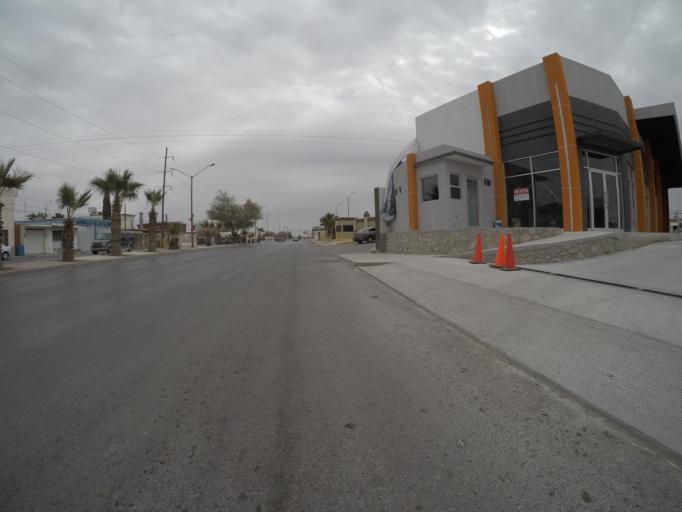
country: MX
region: Chihuahua
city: Ciudad Juarez
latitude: 31.7397
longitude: -106.4229
